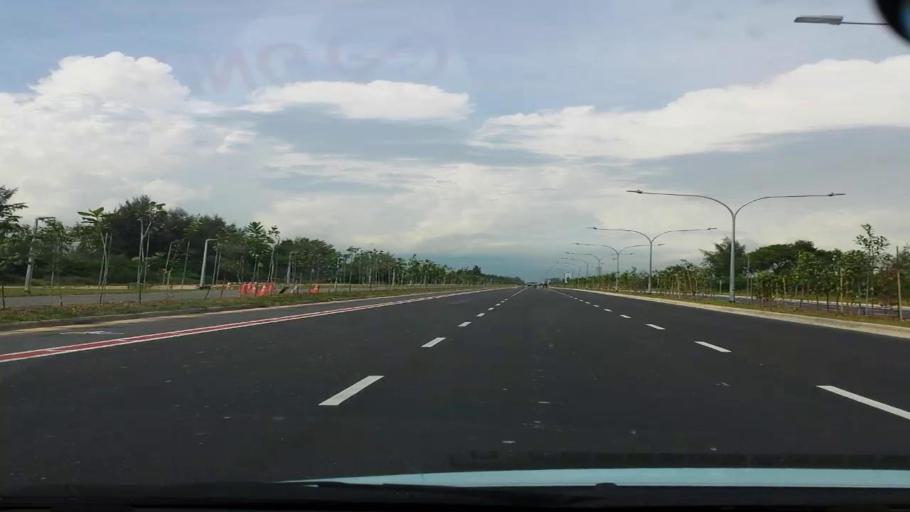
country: SG
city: Singapore
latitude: 1.3517
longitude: 104.0298
